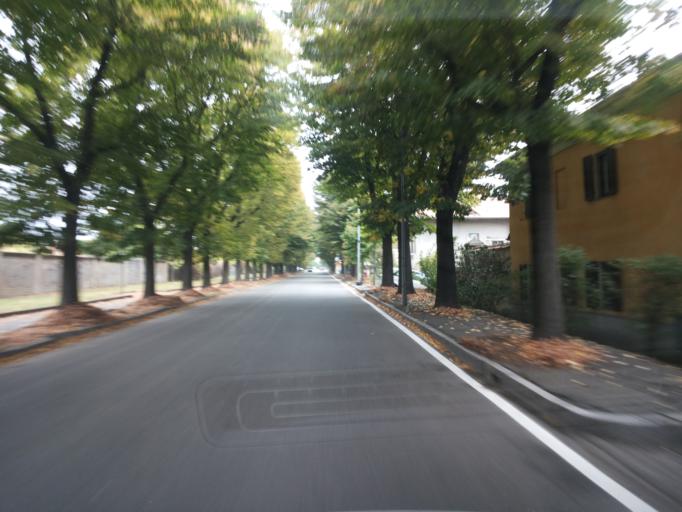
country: IT
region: Piedmont
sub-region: Provincia di Vercelli
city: Vercelli
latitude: 45.3329
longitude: 8.4351
